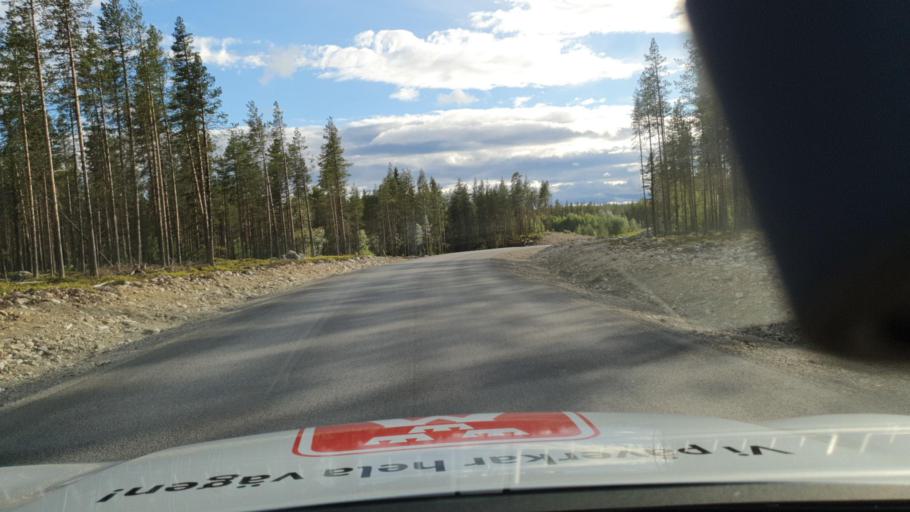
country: SE
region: Vaesterbotten
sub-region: Storumans Kommun
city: Storuman
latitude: 65.0735
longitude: 17.1085
